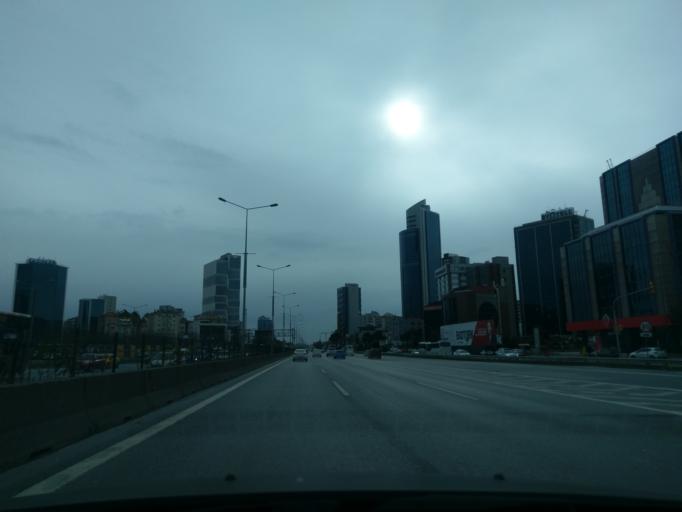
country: TR
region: Istanbul
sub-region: Atasehir
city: Atasehir
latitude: 40.9776
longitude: 29.0976
